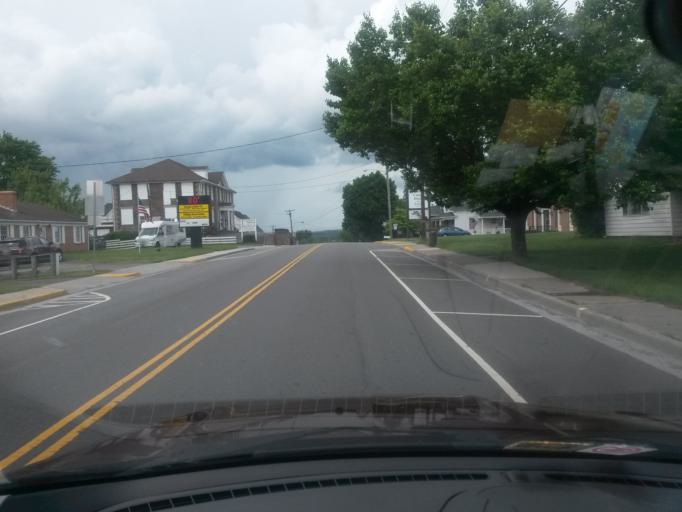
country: US
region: Virginia
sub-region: Floyd County
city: Floyd
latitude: 36.9131
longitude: -80.3206
